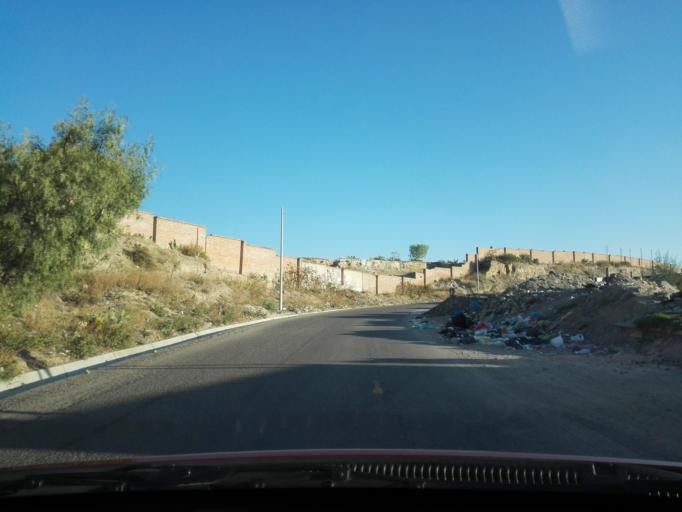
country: PE
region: Ayacucho
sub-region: Provincia de Huamanga
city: Ayacucho
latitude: -13.1394
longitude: -74.2226
